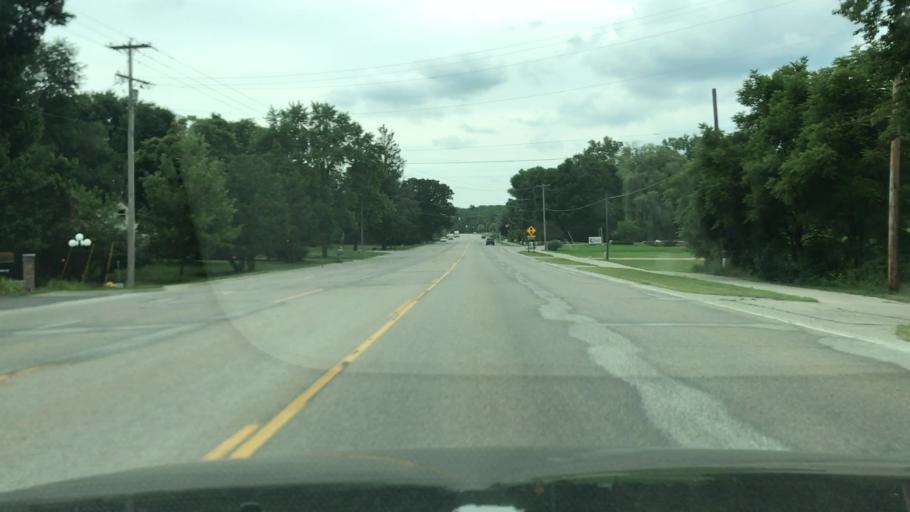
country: US
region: Michigan
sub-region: Kent County
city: Forest Hills
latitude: 42.9177
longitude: -85.5028
